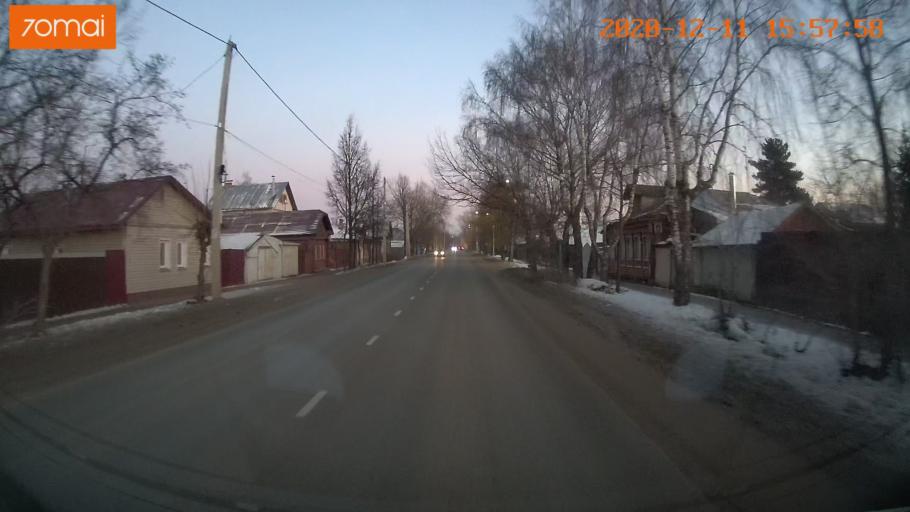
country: RU
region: Ivanovo
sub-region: Gorod Ivanovo
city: Ivanovo
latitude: 56.9811
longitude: 40.9474
